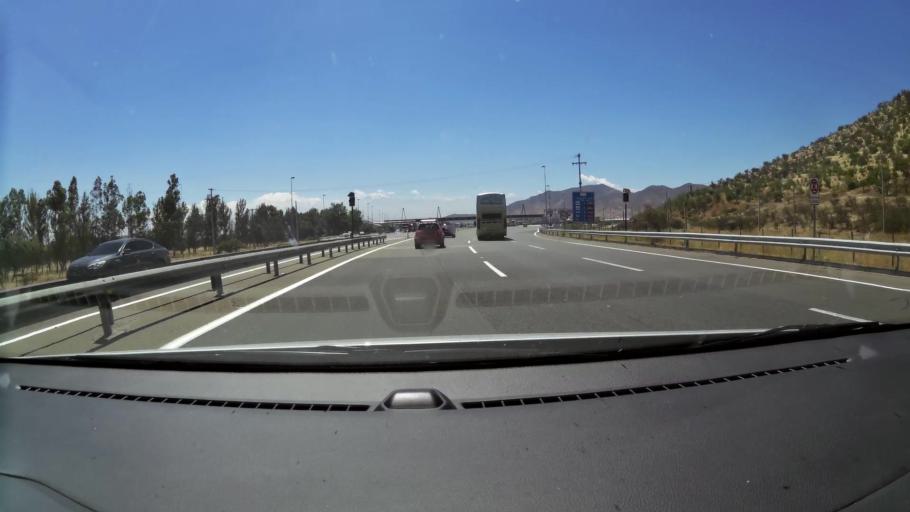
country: CL
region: Santiago Metropolitan
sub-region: Provincia de Talagante
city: Penaflor
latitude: -33.4576
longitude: -70.9017
